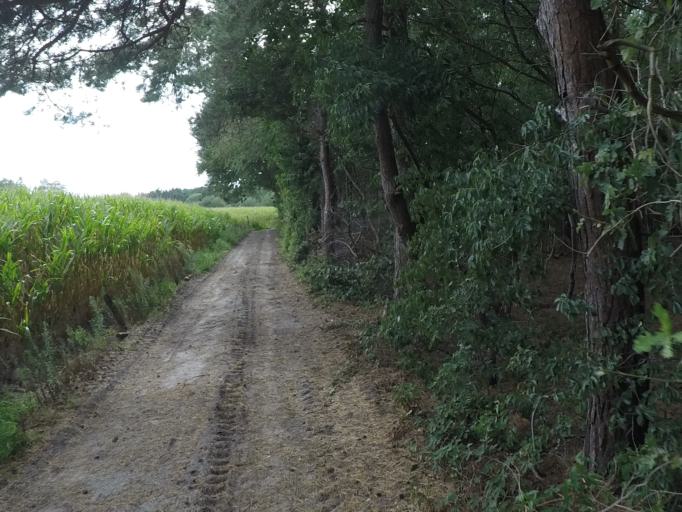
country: BE
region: Flanders
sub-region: Provincie Antwerpen
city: Vorselaar
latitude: 51.2218
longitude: 4.7731
